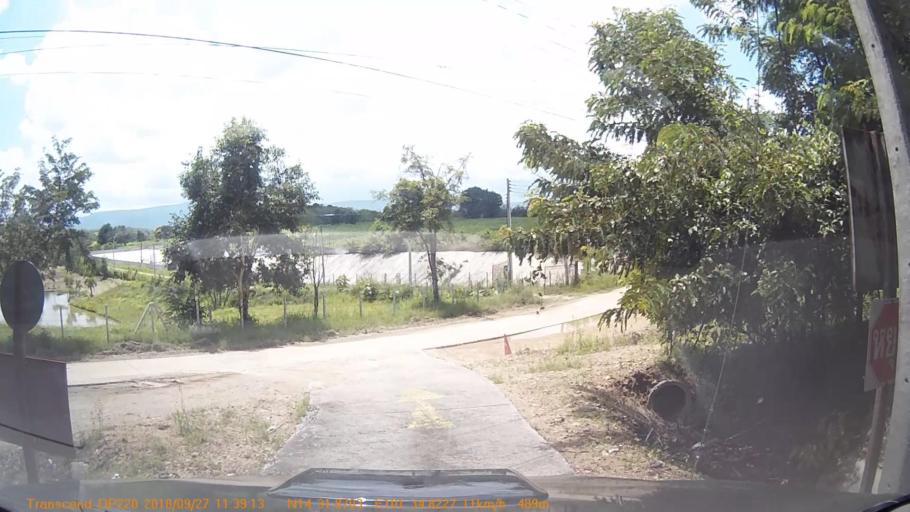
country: TH
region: Nakhon Ratchasima
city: Pak Chong
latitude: 14.5313
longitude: 101.5804
